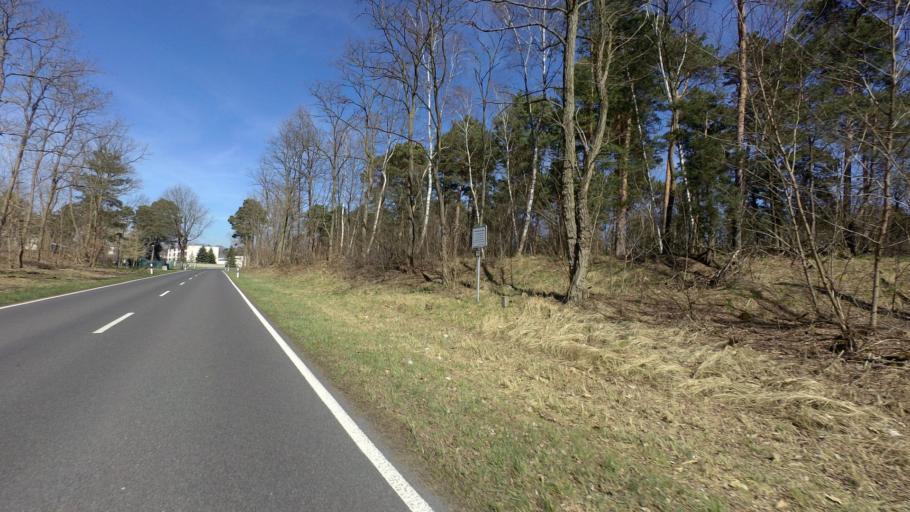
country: DE
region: Brandenburg
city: Storkow
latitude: 52.2339
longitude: 13.9473
